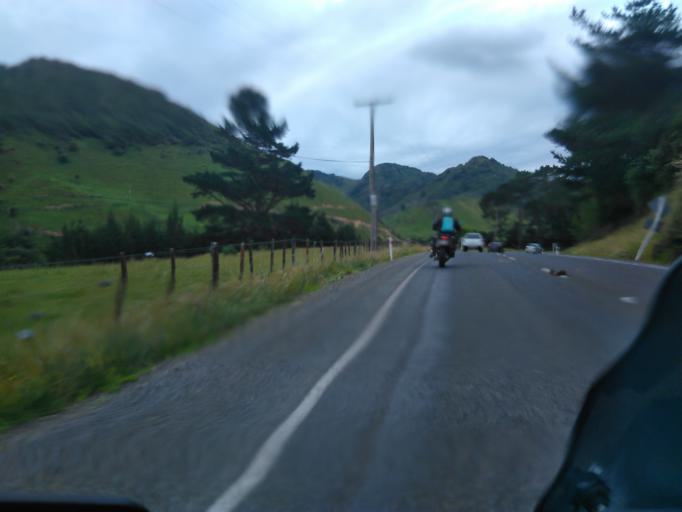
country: NZ
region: Bay of Plenty
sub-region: Opotiki District
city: Opotiki
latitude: -38.3705
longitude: 177.4872
